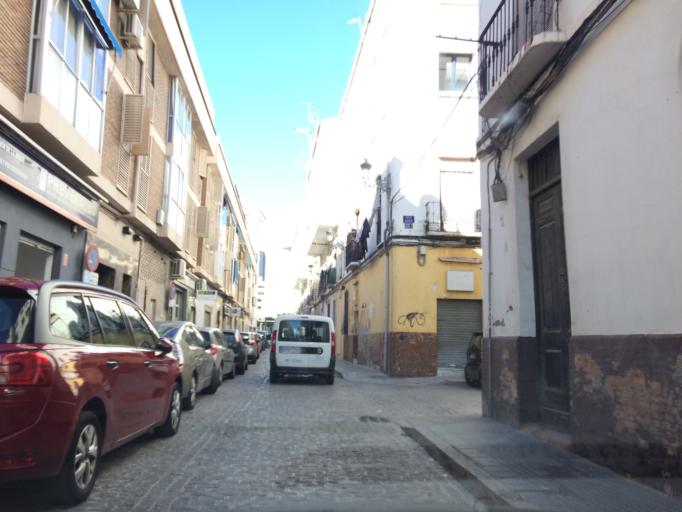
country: ES
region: Andalusia
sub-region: Provincia de Malaga
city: Malaga
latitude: 36.7146
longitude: -4.4290
